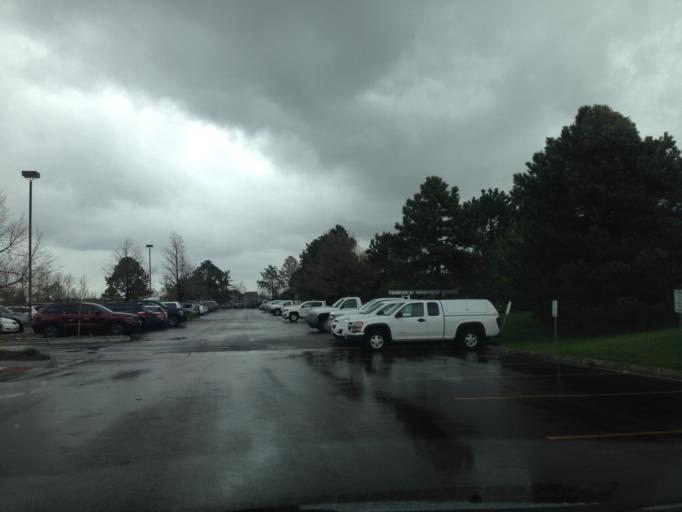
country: US
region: Colorado
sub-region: Adams County
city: Westminster
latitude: 39.8614
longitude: -105.0471
